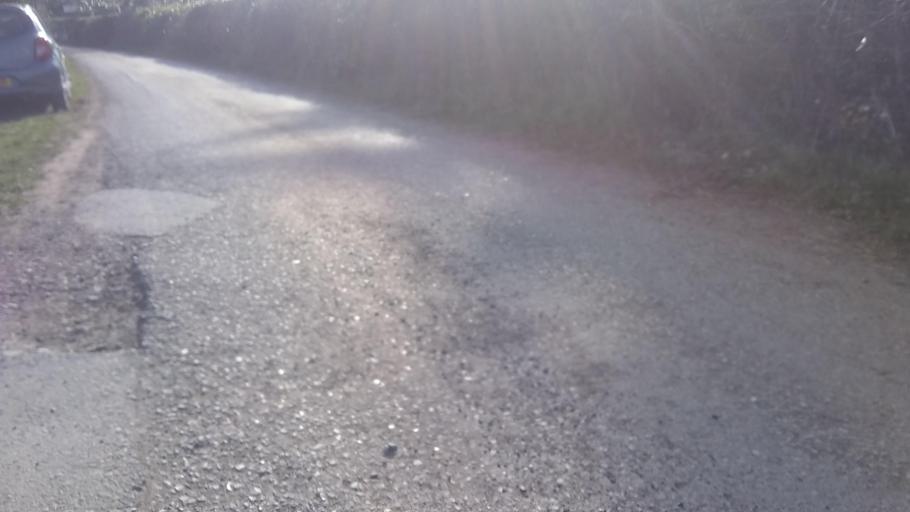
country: GB
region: England
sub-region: Worcestershire
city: Bewdley
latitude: 52.3698
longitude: -2.3936
